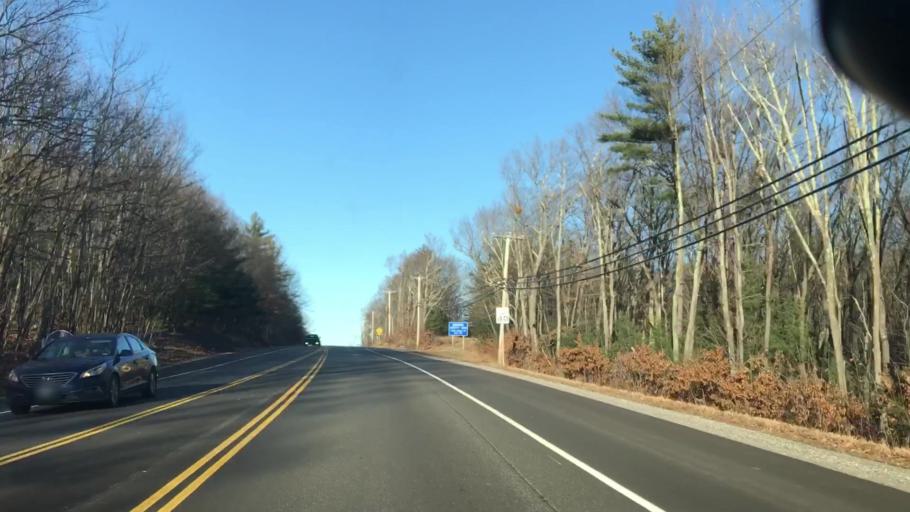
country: US
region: New Hampshire
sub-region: Hillsborough County
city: Bedford
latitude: 42.9241
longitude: -71.5350
